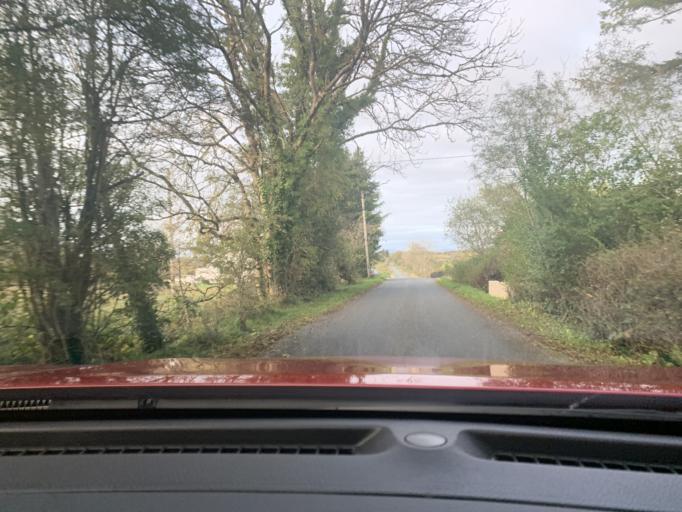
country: IE
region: Connaught
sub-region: Roscommon
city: Ballaghaderreen
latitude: 53.9926
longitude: -8.6102
